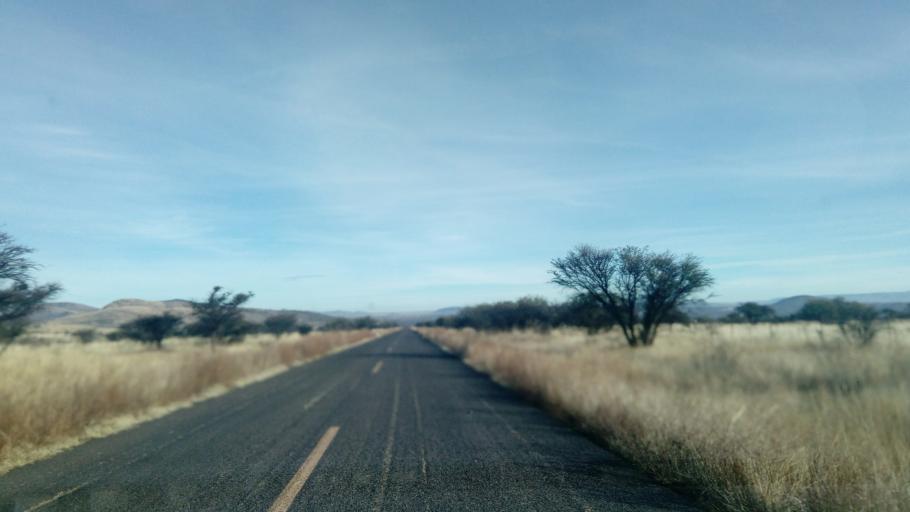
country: MX
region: Durango
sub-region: Nombre de Dios
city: Nombre de Dios
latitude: 23.9247
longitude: -104.3349
